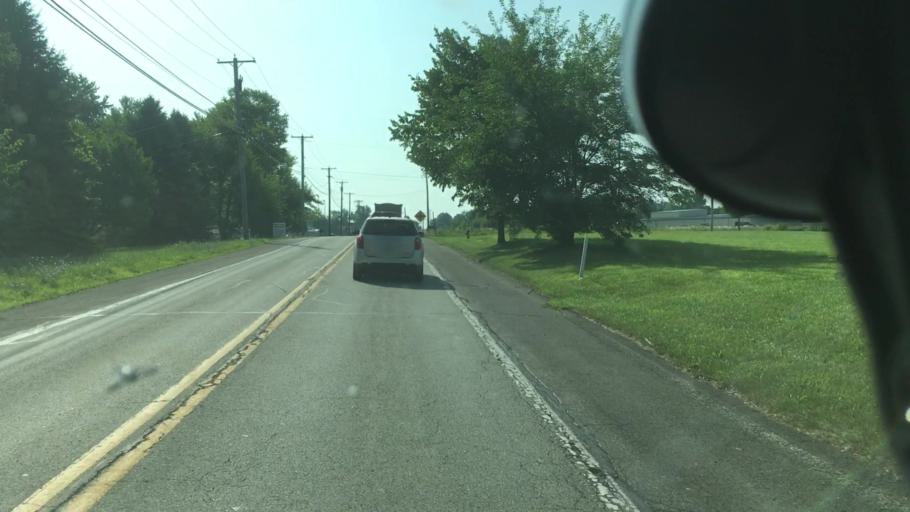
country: US
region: Pennsylvania
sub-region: Lawrence County
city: Oakwood
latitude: 41.0176
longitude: -80.4102
